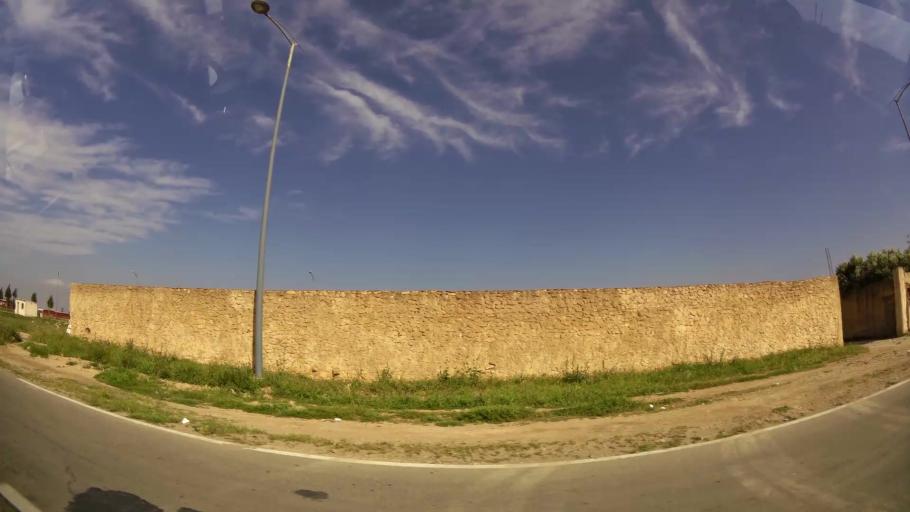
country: MA
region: Oriental
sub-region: Oujda-Angad
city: Oujda
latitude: 34.7237
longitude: -1.8787
